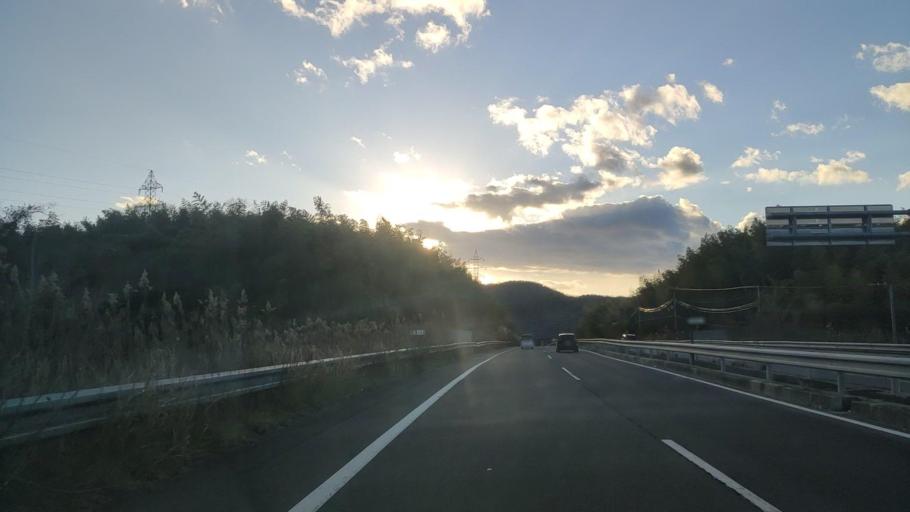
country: JP
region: Hyogo
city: Tatsunocho-tominaga
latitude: 34.8596
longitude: 134.6155
